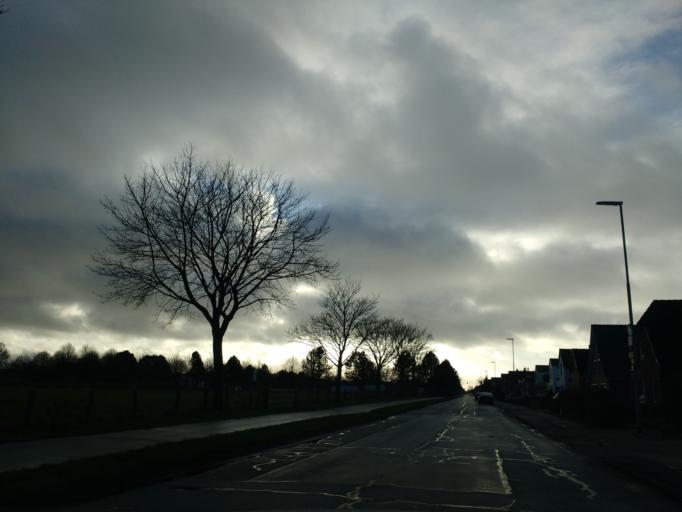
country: DE
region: Schleswig-Holstein
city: Brunsbuttel
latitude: 53.9023
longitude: 9.1337
